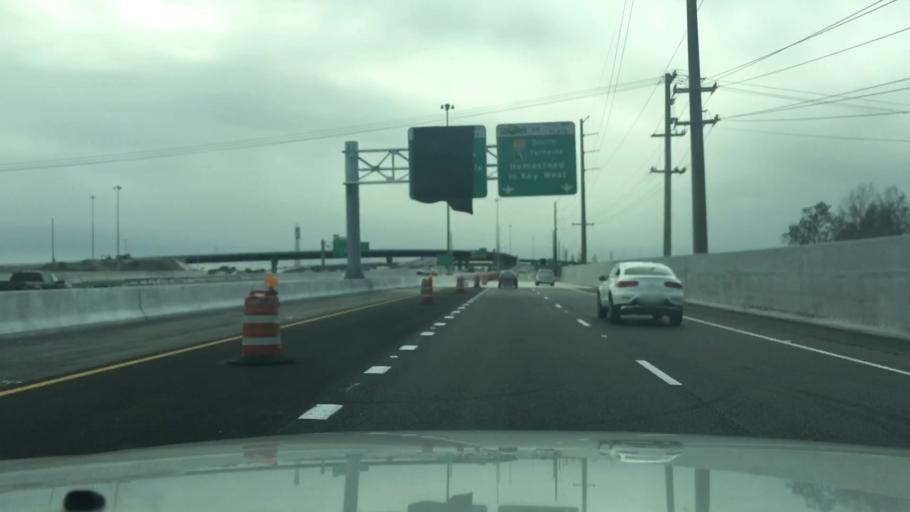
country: US
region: Florida
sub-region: Miami-Dade County
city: Palm Springs North
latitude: 25.9578
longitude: -80.3523
